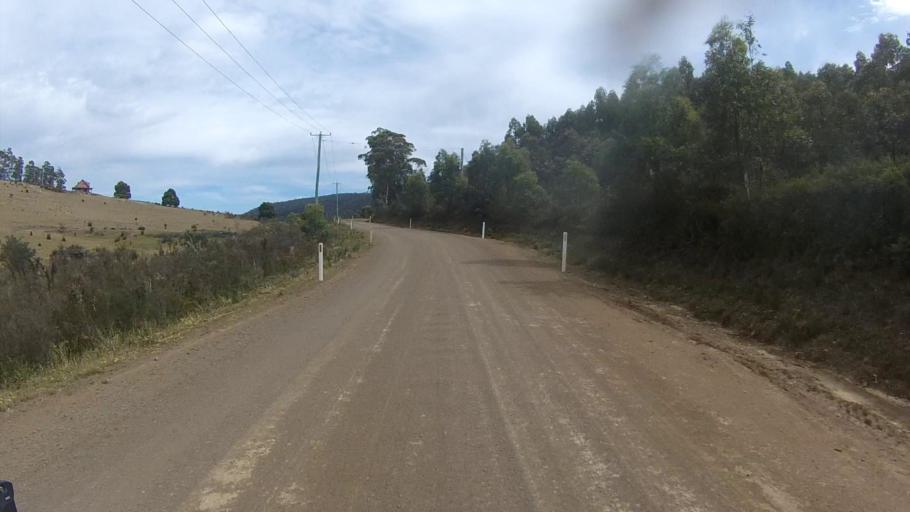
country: AU
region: Tasmania
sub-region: Sorell
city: Sorell
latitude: -42.7584
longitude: 147.8011
